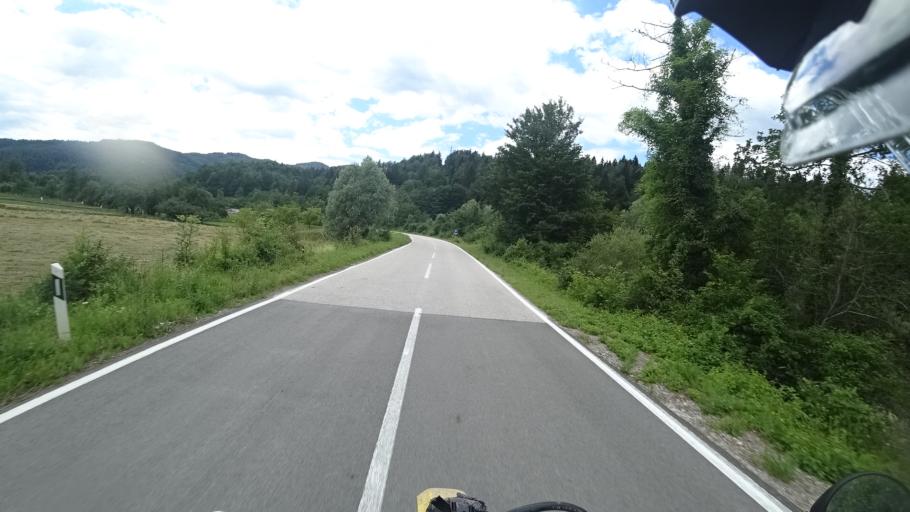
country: SI
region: Osilnica
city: Osilnica
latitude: 45.5346
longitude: 14.7045
